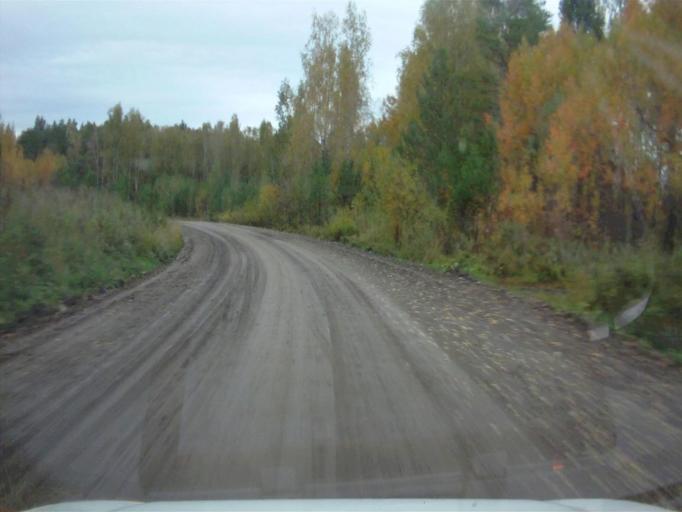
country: RU
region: Chelyabinsk
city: Nyazepetrovsk
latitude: 56.1205
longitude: 59.3695
